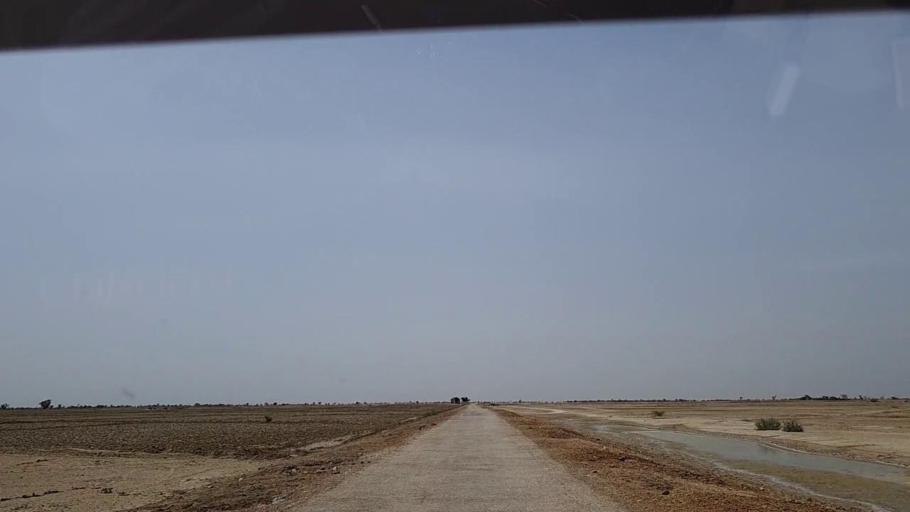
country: PK
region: Sindh
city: Johi
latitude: 26.7269
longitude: 67.6409
